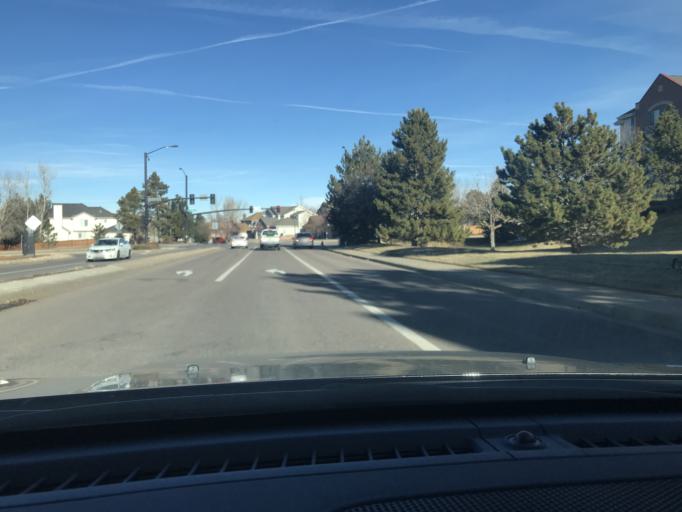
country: US
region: Colorado
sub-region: Arapahoe County
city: Centennial
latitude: 39.6015
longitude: -104.8808
